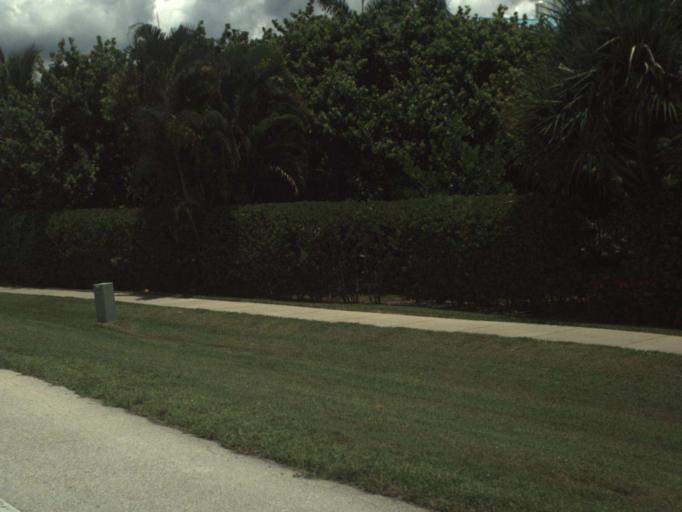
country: US
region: Florida
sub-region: Martin County
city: Sewall's Point
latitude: 27.2243
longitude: -80.1808
